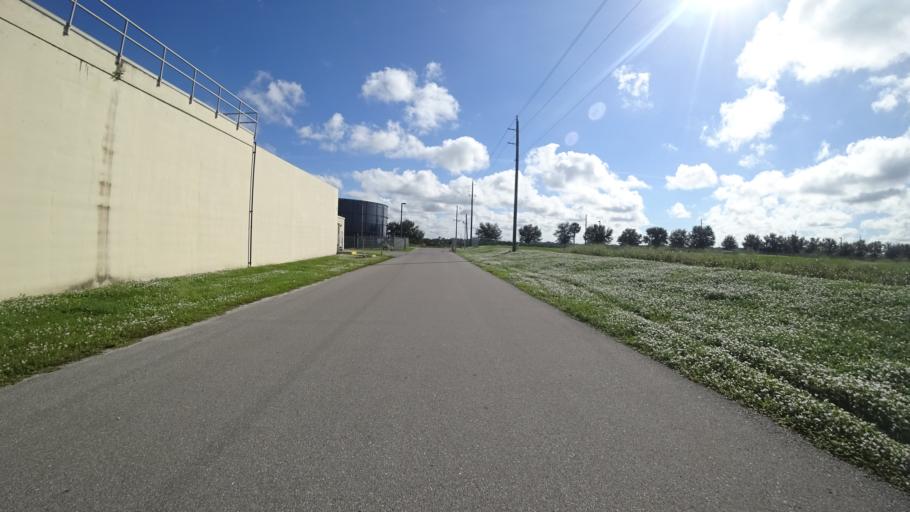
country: US
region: Florida
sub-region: Manatee County
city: Ellenton
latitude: 27.5841
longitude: -82.4756
